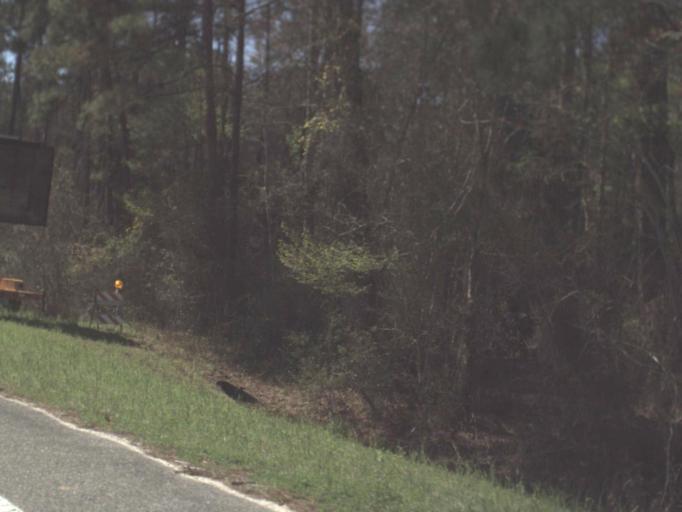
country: US
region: Florida
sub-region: Calhoun County
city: Blountstown
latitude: 30.5475
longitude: -85.0254
